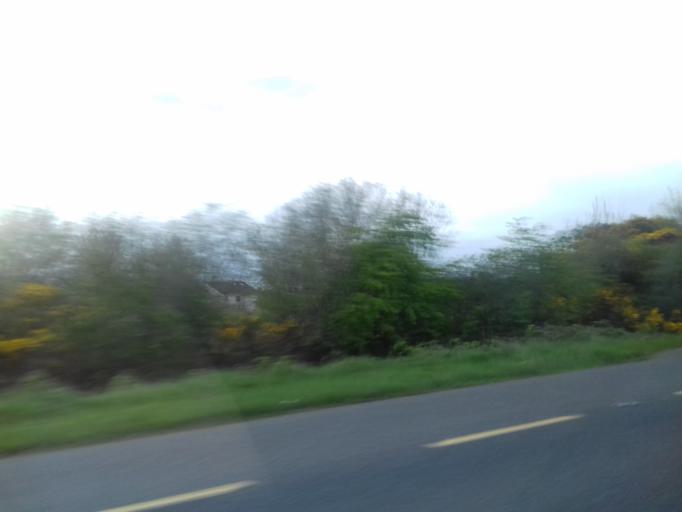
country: IE
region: Ulster
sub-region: An Cabhan
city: Cavan
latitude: 54.0040
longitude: -7.3440
